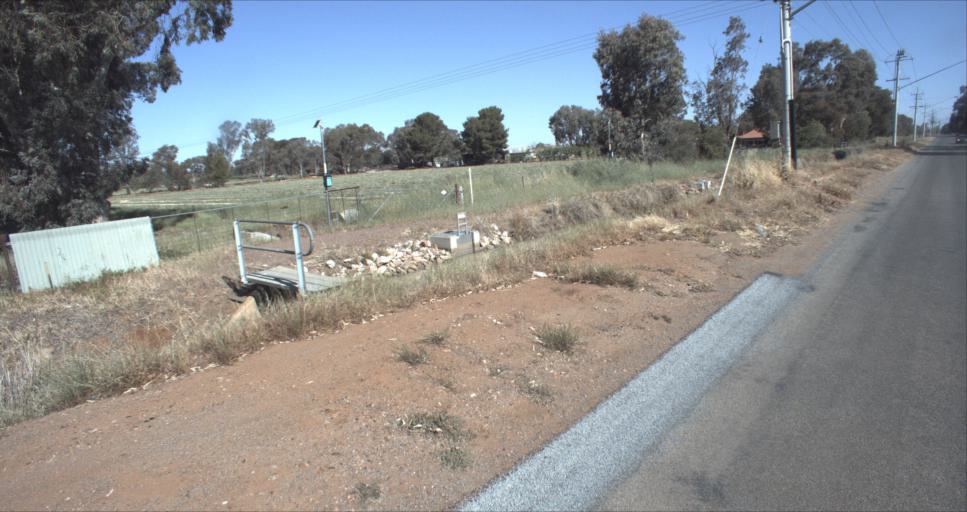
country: AU
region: New South Wales
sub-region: Leeton
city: Leeton
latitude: -34.5663
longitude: 146.4144
